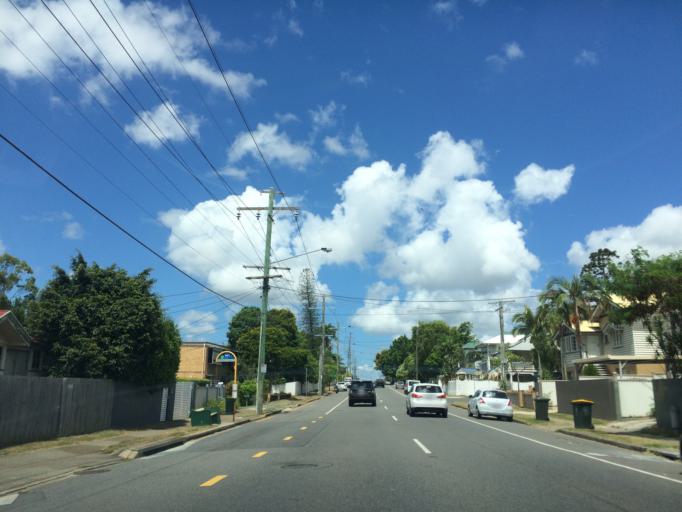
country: AU
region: Queensland
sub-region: Brisbane
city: Woolloongabba
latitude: -27.4861
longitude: 153.0461
